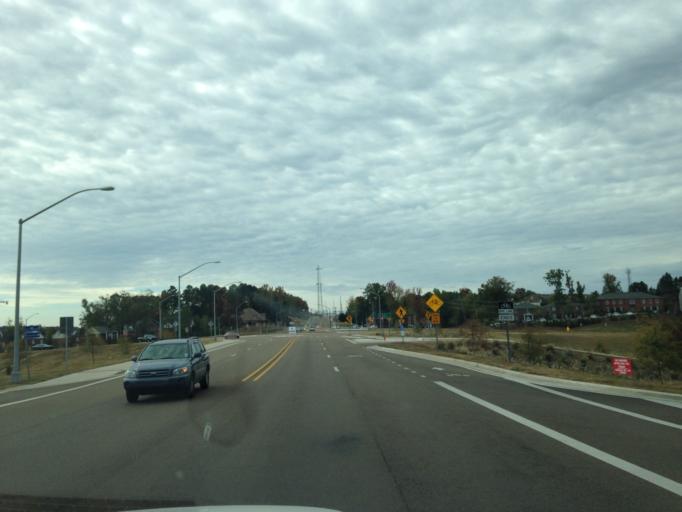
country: US
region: Mississippi
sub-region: Lafayette County
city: University
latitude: 34.3573
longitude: -89.5321
